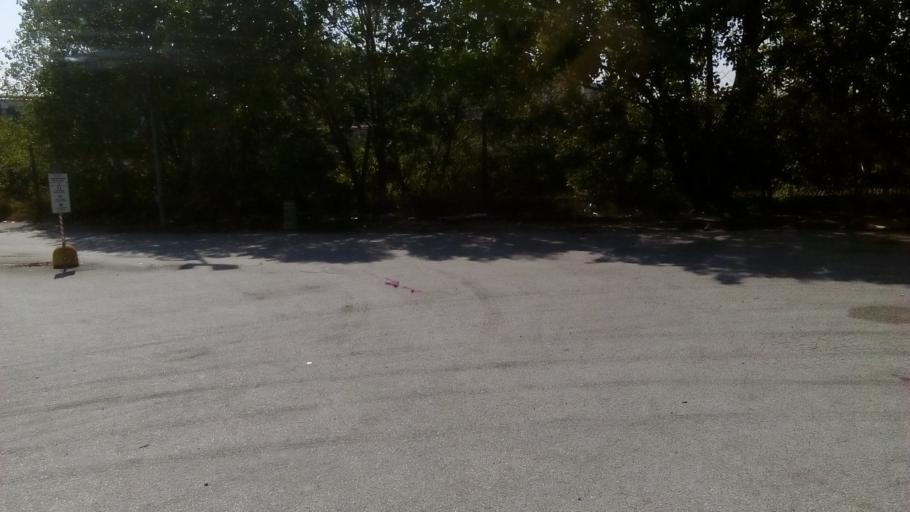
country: IT
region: Veneto
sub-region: Provincia di Verona
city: Vallese
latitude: 45.3485
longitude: 11.0723
